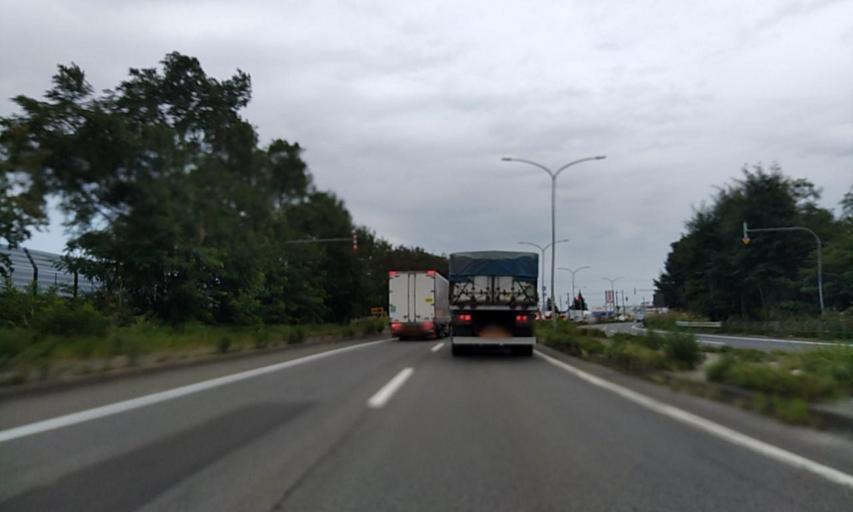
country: JP
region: Hokkaido
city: Ishikari
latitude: 43.1596
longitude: 141.2478
